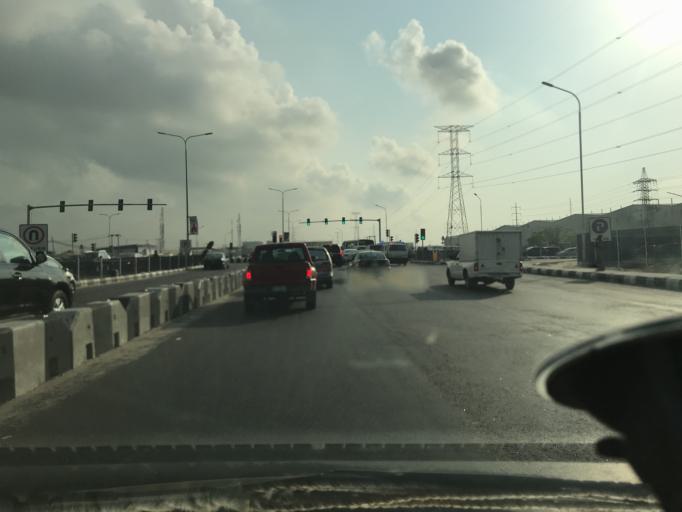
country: NG
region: Lagos
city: Ikoyi
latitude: 6.4327
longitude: 3.4813
